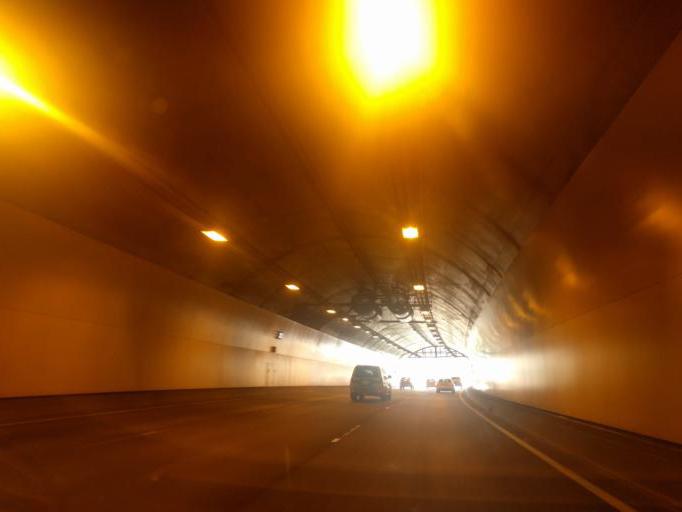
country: AU
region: South Australia
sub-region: Burnside
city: Mount Osmond
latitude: -34.9740
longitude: 138.6771
